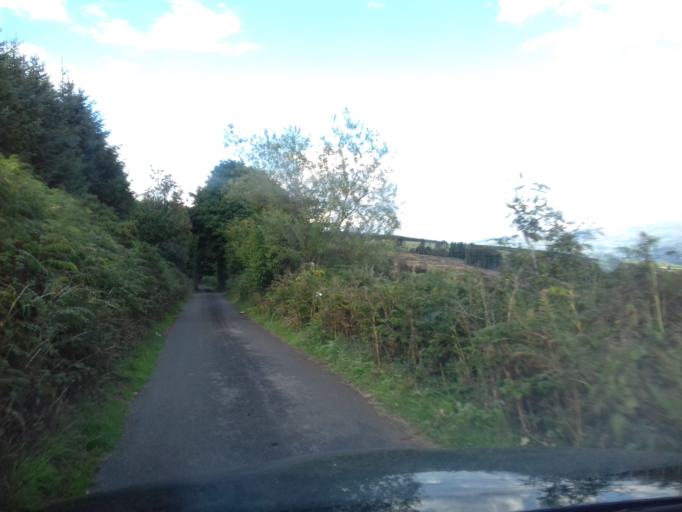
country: IE
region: Leinster
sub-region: Kilkenny
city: Graiguenamanagh
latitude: 52.5545
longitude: -7.0179
